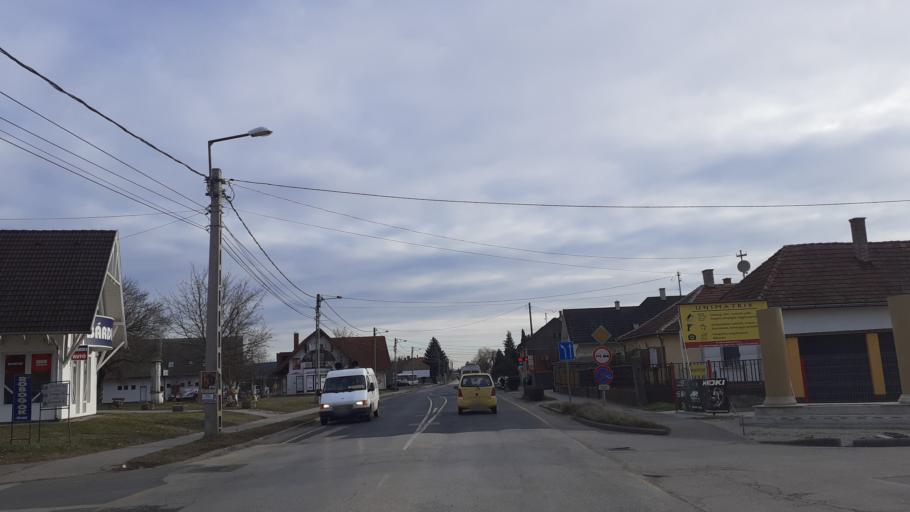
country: HU
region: Fejer
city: Sarbogard
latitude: 46.8813
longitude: 18.6224
